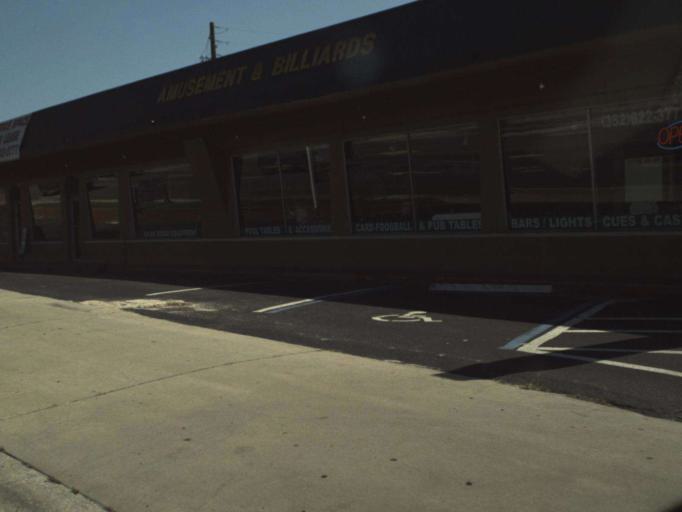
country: US
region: Florida
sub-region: Marion County
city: Ocala
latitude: 29.1681
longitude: -82.1382
